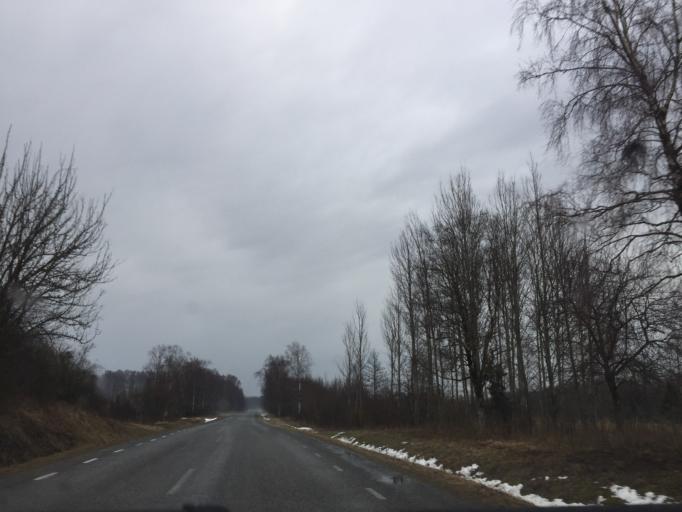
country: EE
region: Saare
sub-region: Orissaare vald
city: Orissaare
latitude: 58.5723
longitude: 23.0318
